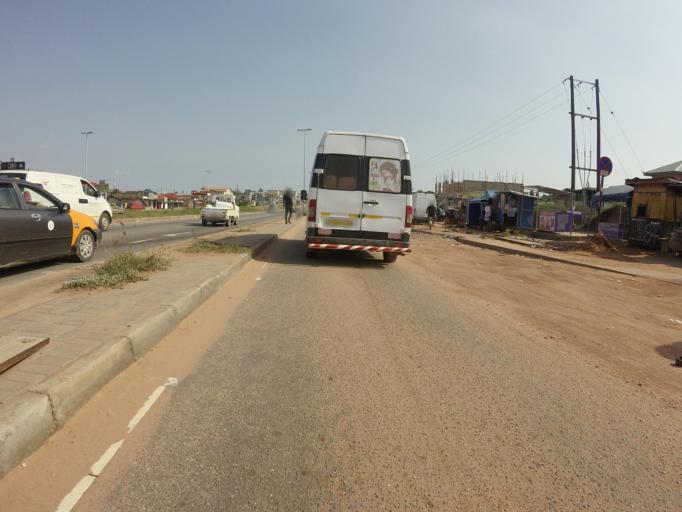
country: GH
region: Greater Accra
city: Gbawe
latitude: 5.6027
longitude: -0.2933
